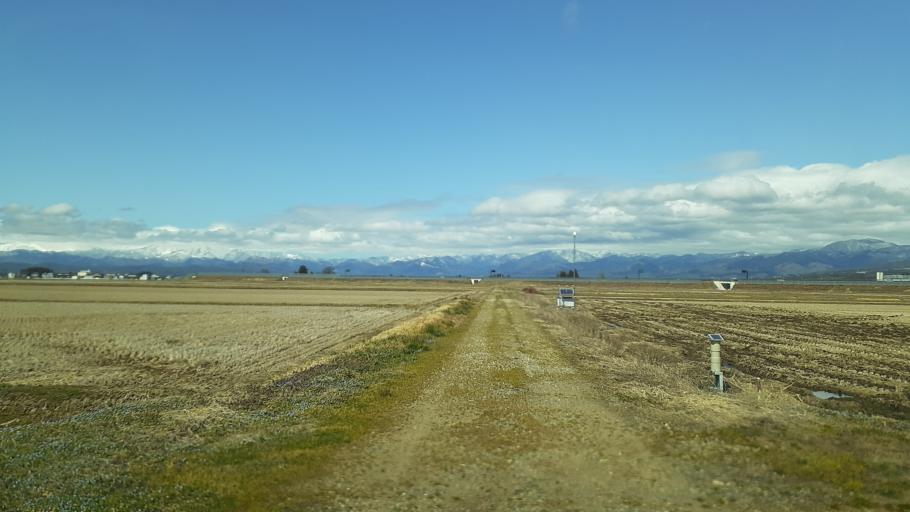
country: JP
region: Fukushima
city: Kitakata
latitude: 37.5458
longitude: 139.9031
